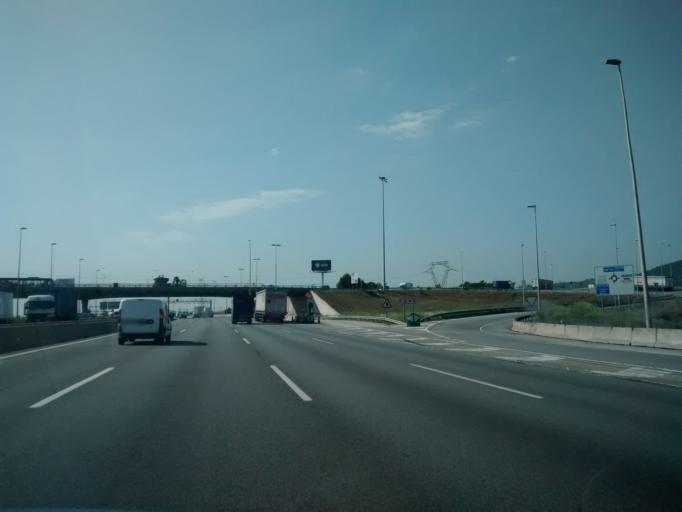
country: ES
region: Catalonia
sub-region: Provincia de Barcelona
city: Sant Vicenc dels Horts
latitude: 41.3943
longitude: 2.0237
